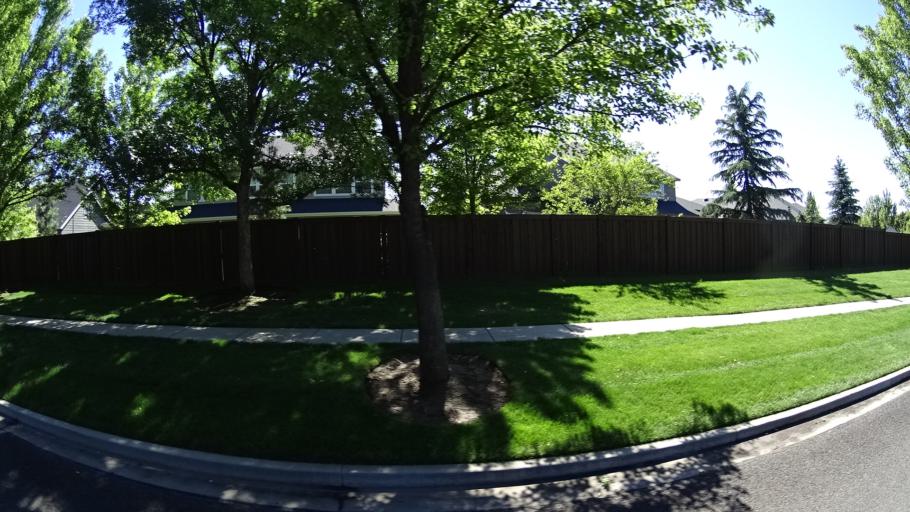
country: US
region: Idaho
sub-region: Ada County
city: Meridian
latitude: 43.6585
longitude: -116.4012
